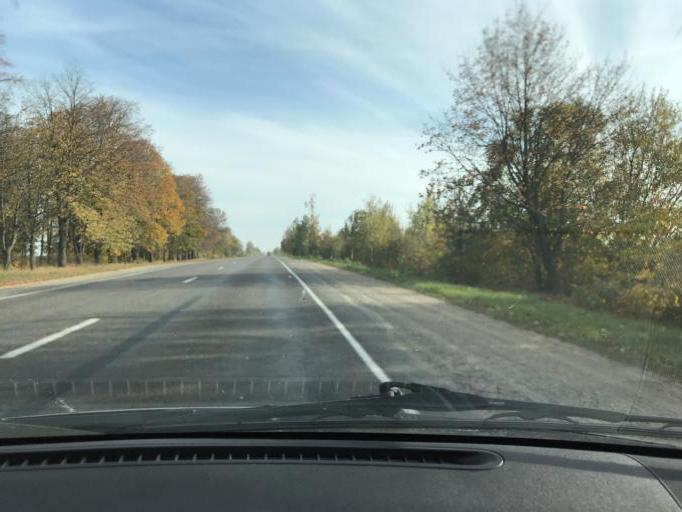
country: BY
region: Brest
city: Asnyezhytsy
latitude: 52.2158
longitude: 26.0401
